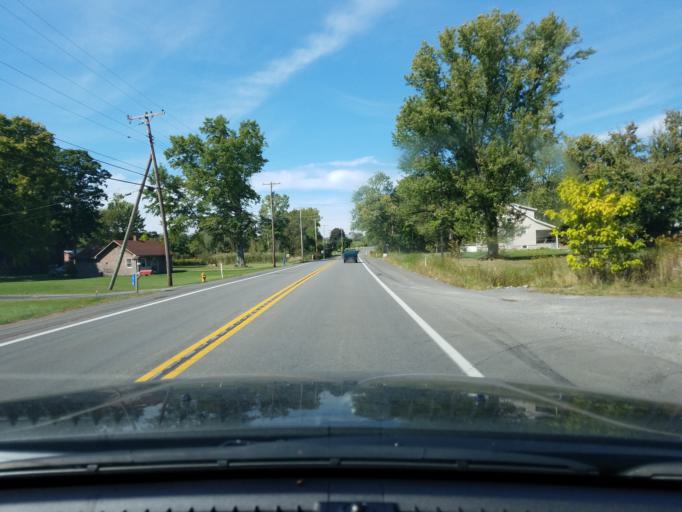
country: US
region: Pennsylvania
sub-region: Lawrence County
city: Ellwood City
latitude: 40.9455
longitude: -80.2836
